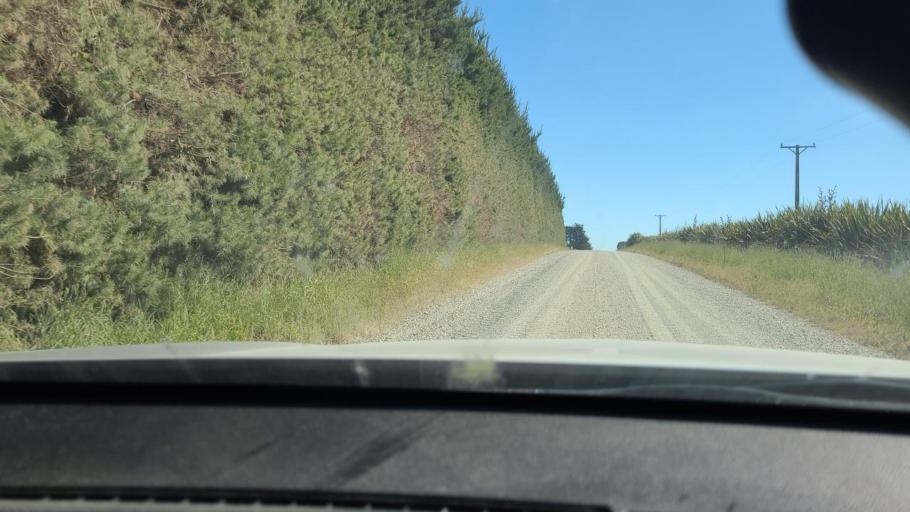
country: NZ
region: Southland
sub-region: Southland District
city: Winton
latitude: -46.2676
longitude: 168.2201
